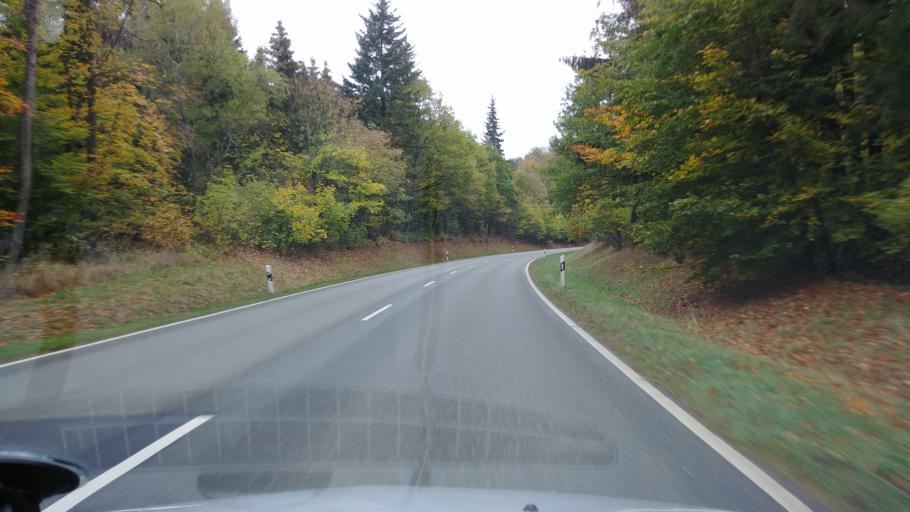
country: DE
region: Hesse
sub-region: Regierungsbezirk Darmstadt
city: Bad Schwalbach
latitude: 50.1171
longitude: 8.0543
